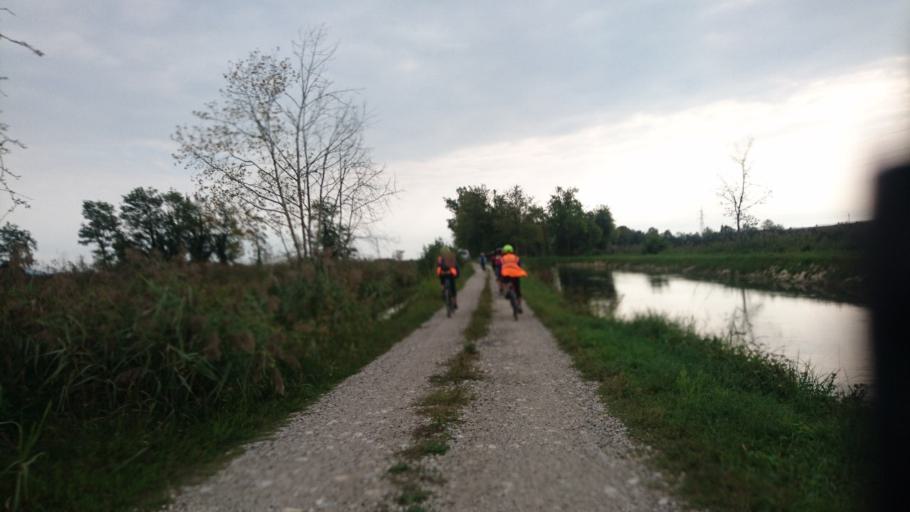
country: IT
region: Veneto
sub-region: Provincia di Verona
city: Monticelli-Fontana
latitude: 45.4029
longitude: 11.1282
